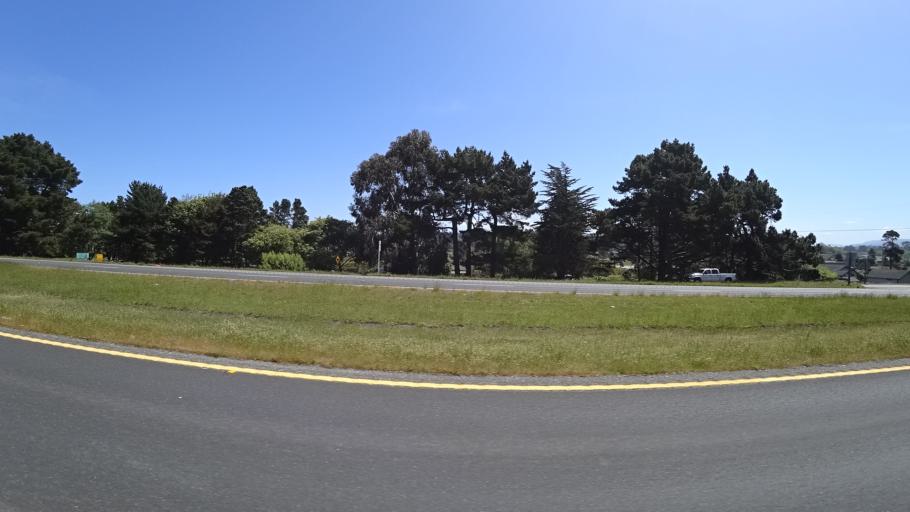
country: US
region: California
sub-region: Humboldt County
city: McKinleyville
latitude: 40.9678
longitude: -124.1161
